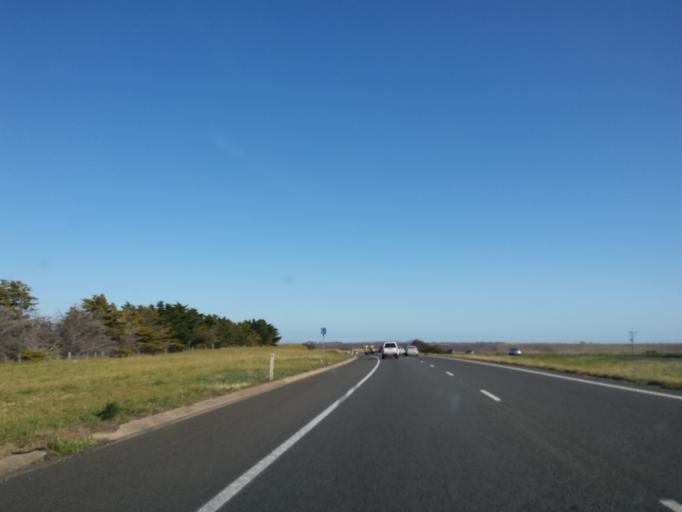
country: AU
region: Victoria
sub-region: Moorabool
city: Bacchus Marsh
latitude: -37.6491
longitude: 144.3675
